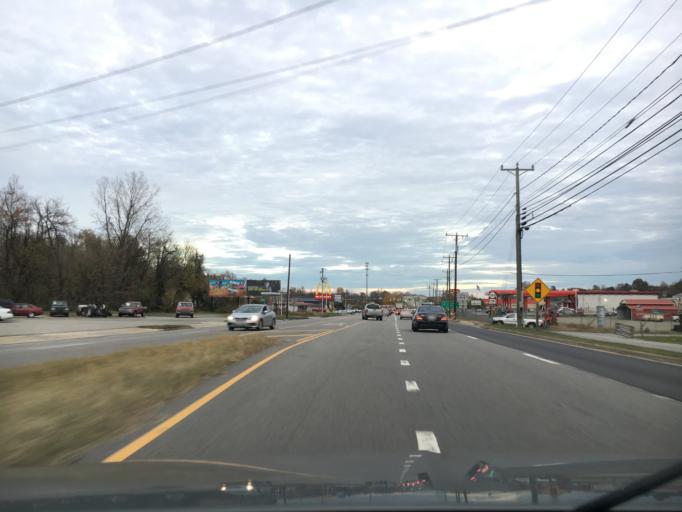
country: US
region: Virginia
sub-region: Halifax County
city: South Boston
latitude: 36.6867
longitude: -78.9028
